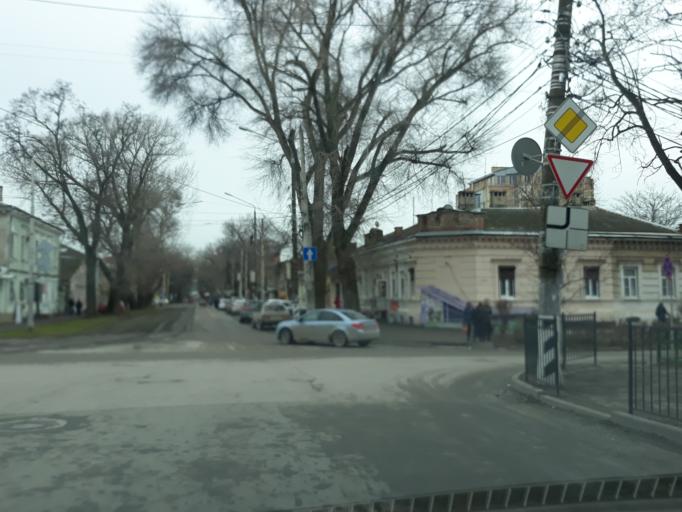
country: RU
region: Rostov
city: Taganrog
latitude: 47.2097
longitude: 38.9313
